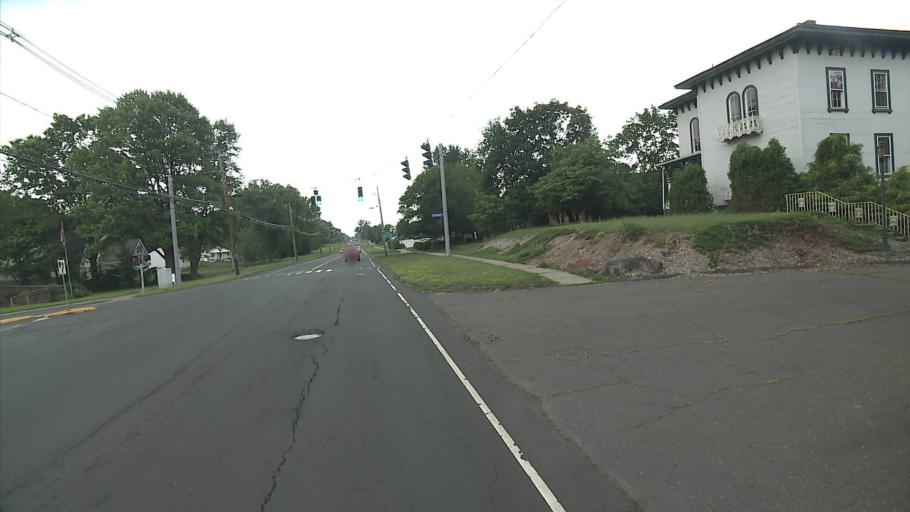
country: US
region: Connecticut
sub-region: Hartford County
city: Newington
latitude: 41.7116
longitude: -72.7367
